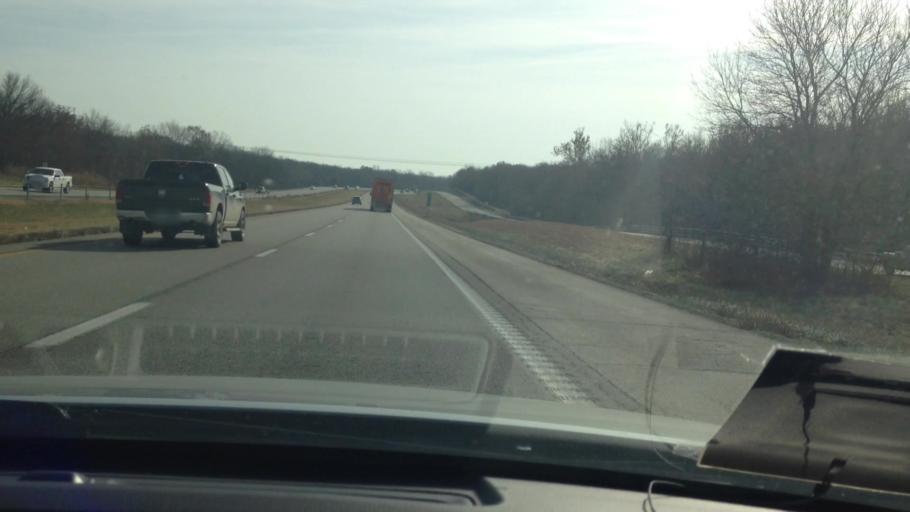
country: US
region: Missouri
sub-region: Cass County
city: Peculiar
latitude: 38.7615
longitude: -94.4879
